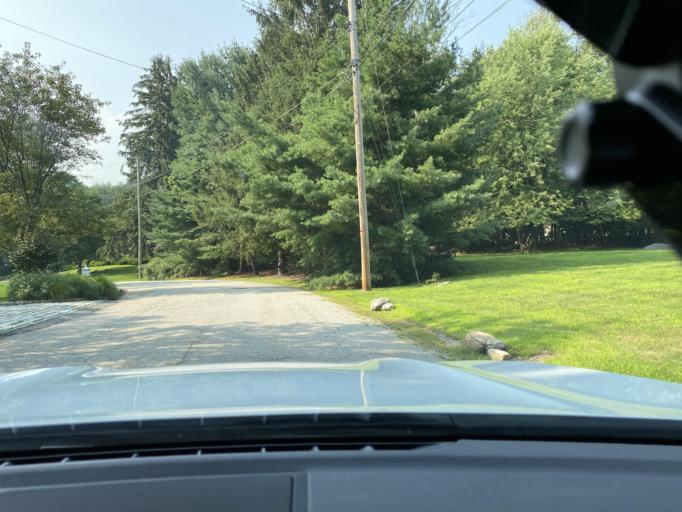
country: US
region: New York
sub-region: Rockland County
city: Airmont
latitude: 41.0858
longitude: -74.1181
